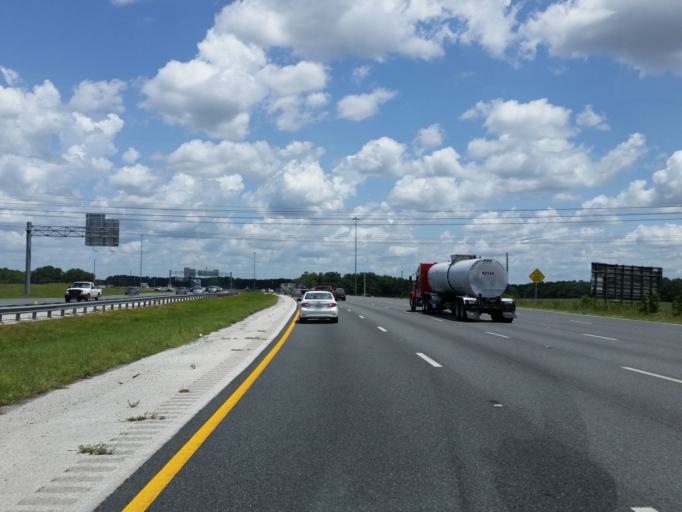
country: US
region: Florida
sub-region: Sumter County
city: Wildwood
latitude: 28.8789
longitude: -82.0926
